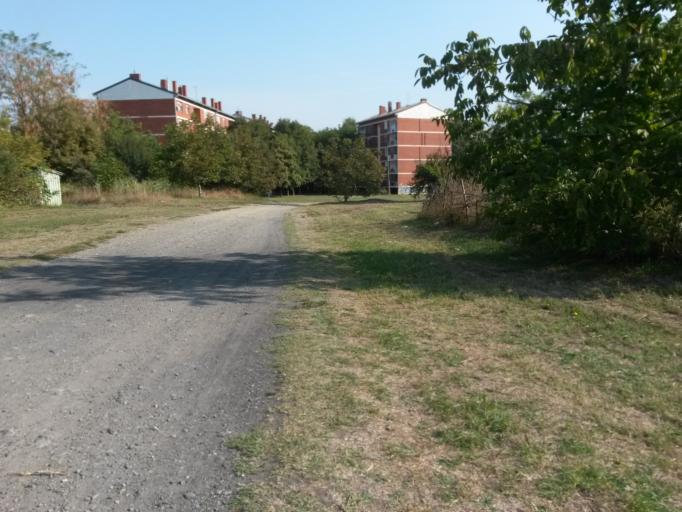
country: HR
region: Osjecko-Baranjska
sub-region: Grad Osijek
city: Osijek
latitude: 45.5429
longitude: 18.7268
